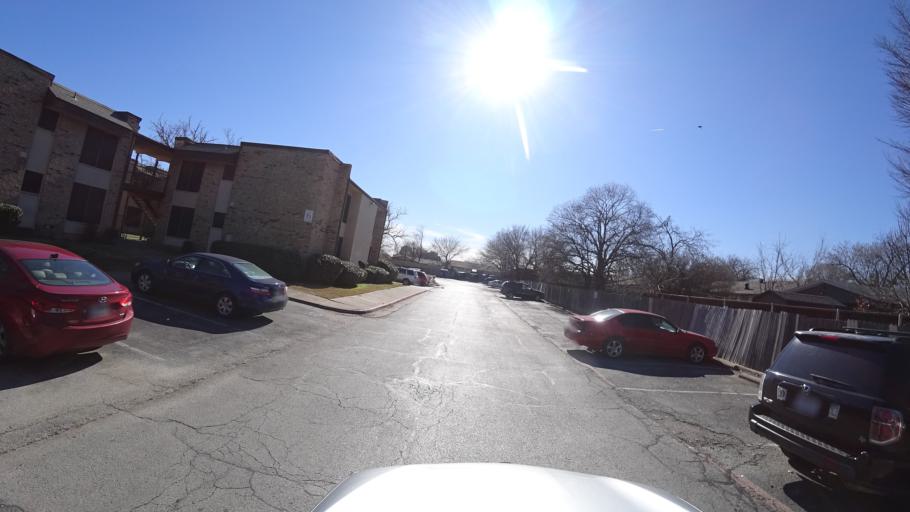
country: US
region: Texas
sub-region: Denton County
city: Lewisville
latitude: 33.0328
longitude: -97.0132
